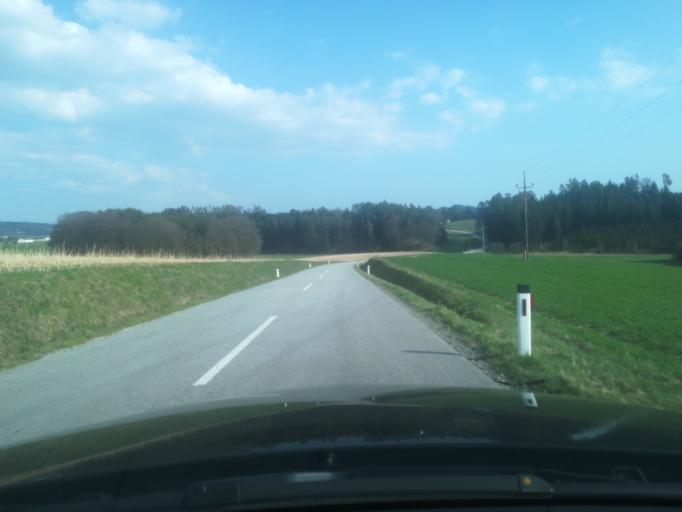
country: AT
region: Upper Austria
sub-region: Politischer Bezirk Perg
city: Perg
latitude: 48.3655
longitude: 14.6501
